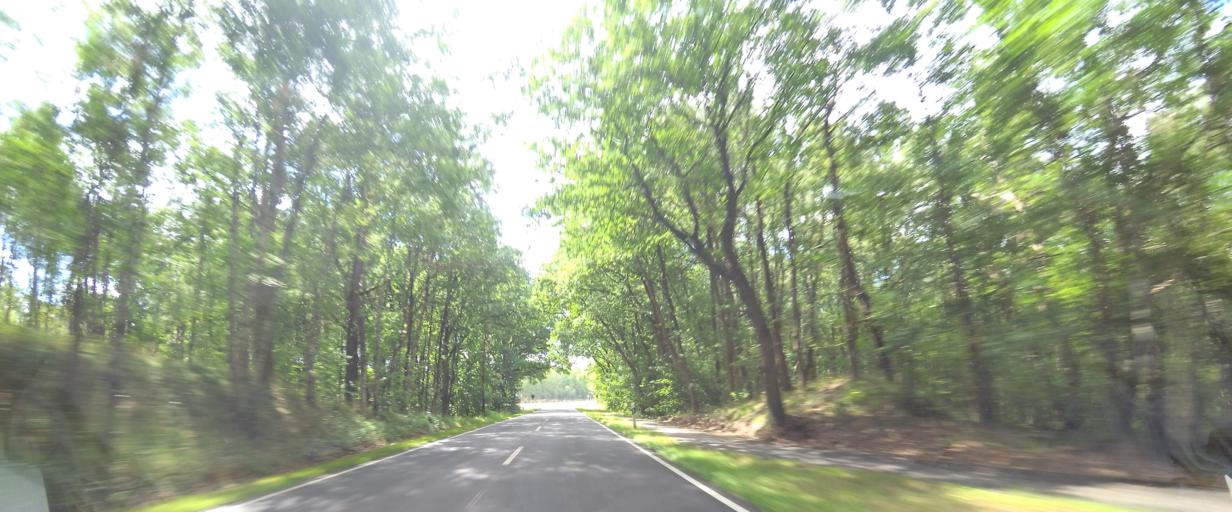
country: DE
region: Lower Saxony
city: Lathen
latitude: 52.8328
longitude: 7.3190
